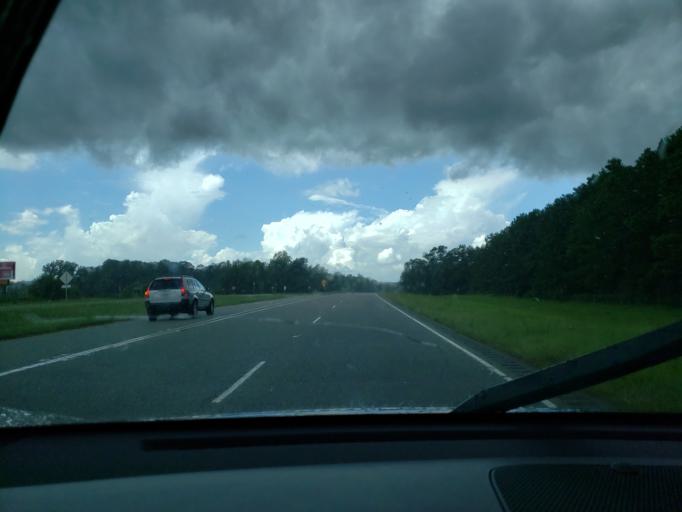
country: US
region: North Carolina
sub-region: Bladen County
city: Elizabethtown
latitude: 34.6057
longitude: -78.6288
